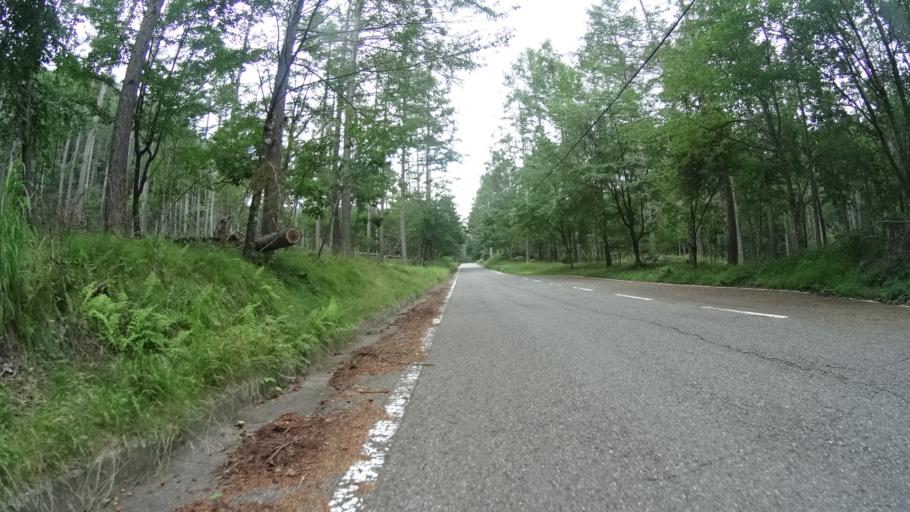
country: JP
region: Yamanashi
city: Kofu-shi
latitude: 35.8849
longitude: 138.5713
